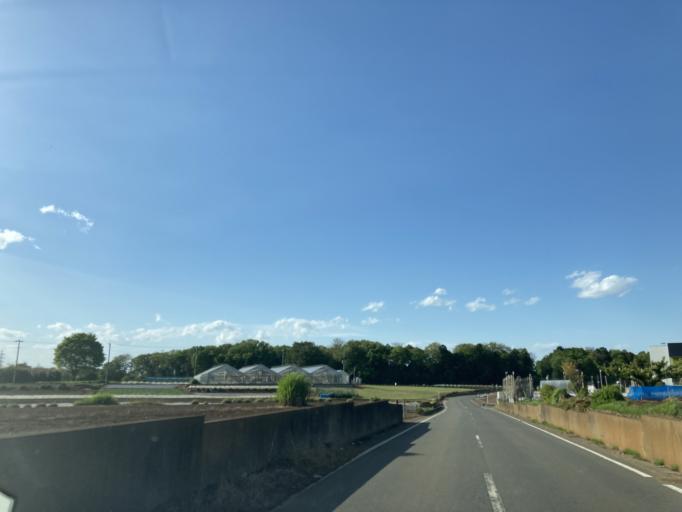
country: JP
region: Saitama
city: Sayama
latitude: 35.8617
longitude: 139.4406
